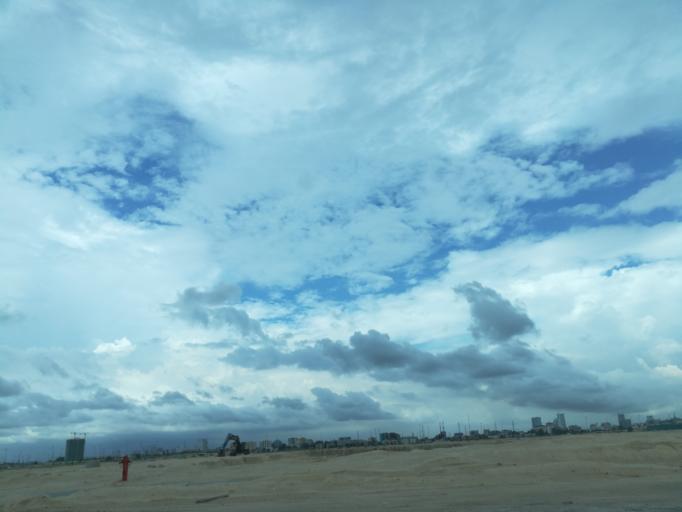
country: NG
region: Lagos
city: Ikoyi
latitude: 6.4072
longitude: 3.4229
